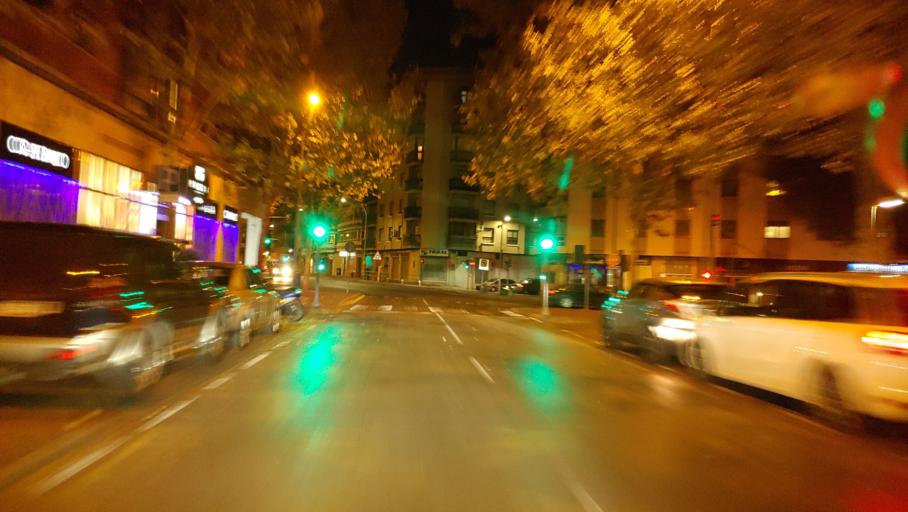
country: ES
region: Castille-La Mancha
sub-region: Provincia de Ciudad Real
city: Ciudad Real
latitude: 38.9797
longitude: -3.9266
